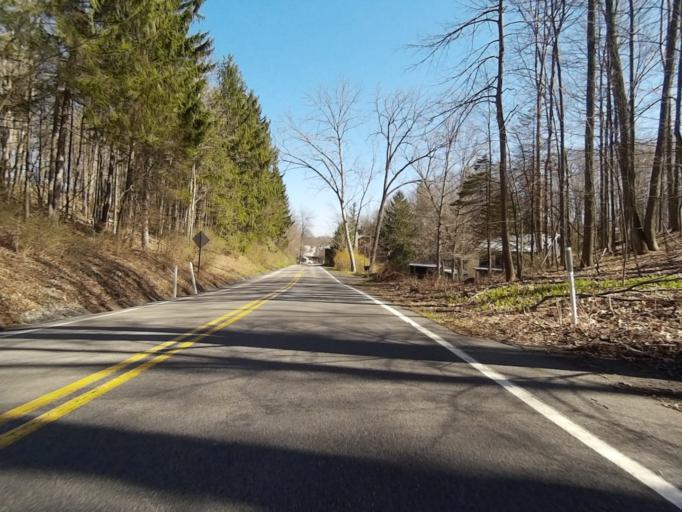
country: US
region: Pennsylvania
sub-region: Centre County
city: Park Forest Village
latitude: 40.8166
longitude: -77.9675
